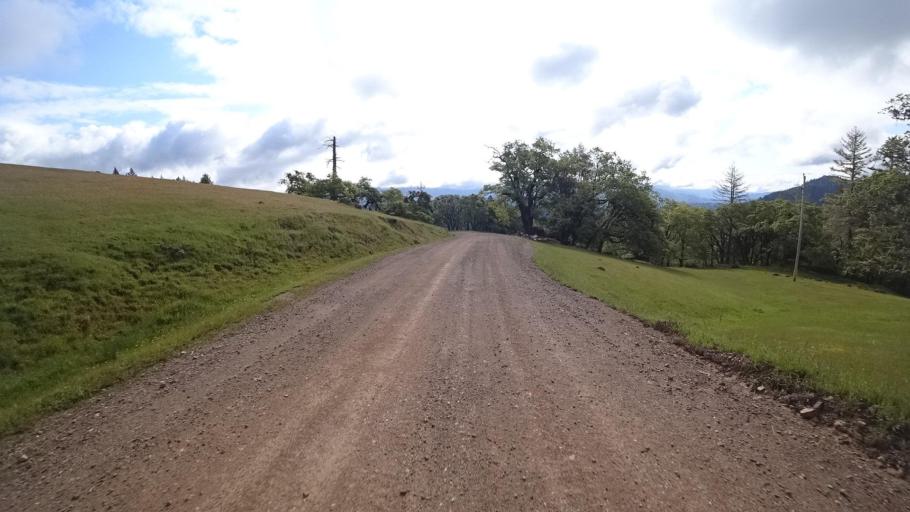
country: US
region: California
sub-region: Humboldt County
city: Redway
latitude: 40.2077
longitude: -123.6882
